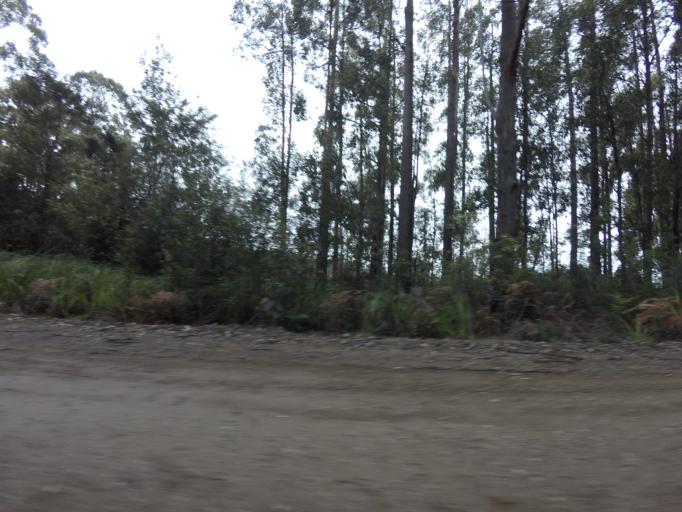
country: AU
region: Tasmania
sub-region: Huon Valley
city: Geeveston
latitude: -43.4823
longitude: 146.8924
